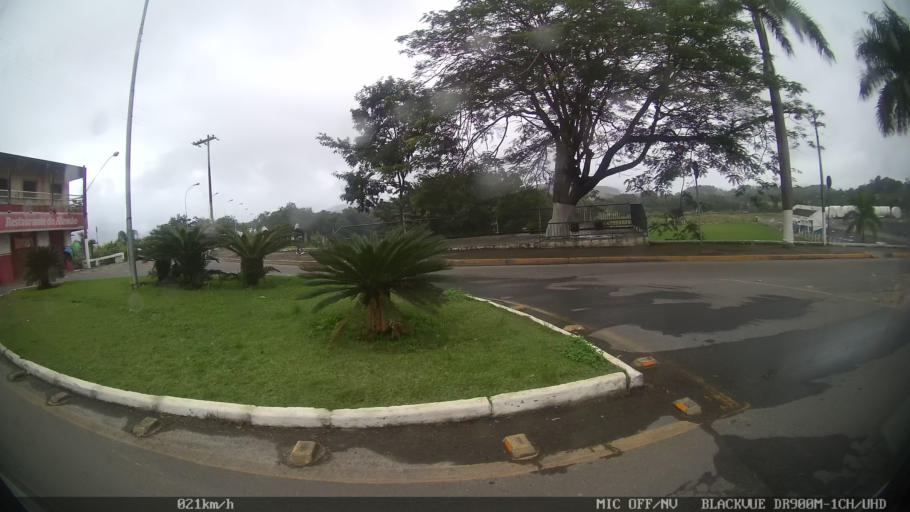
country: BR
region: Sao Paulo
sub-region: Juquia
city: Juquia
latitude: -24.3223
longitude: -47.6358
